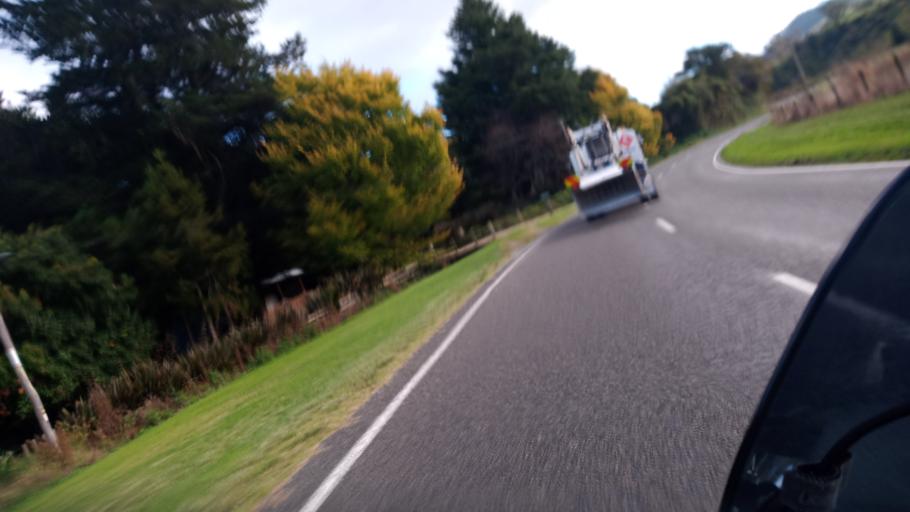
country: NZ
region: Gisborne
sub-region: Gisborne District
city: Gisborne
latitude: -38.5982
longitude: 177.8015
